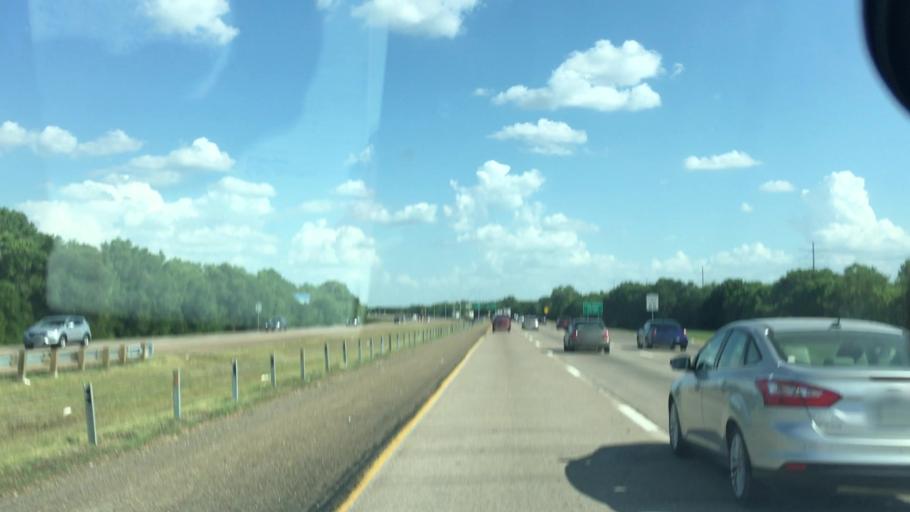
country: US
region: Texas
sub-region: Dallas County
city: Hutchins
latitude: 32.6896
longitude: -96.7489
